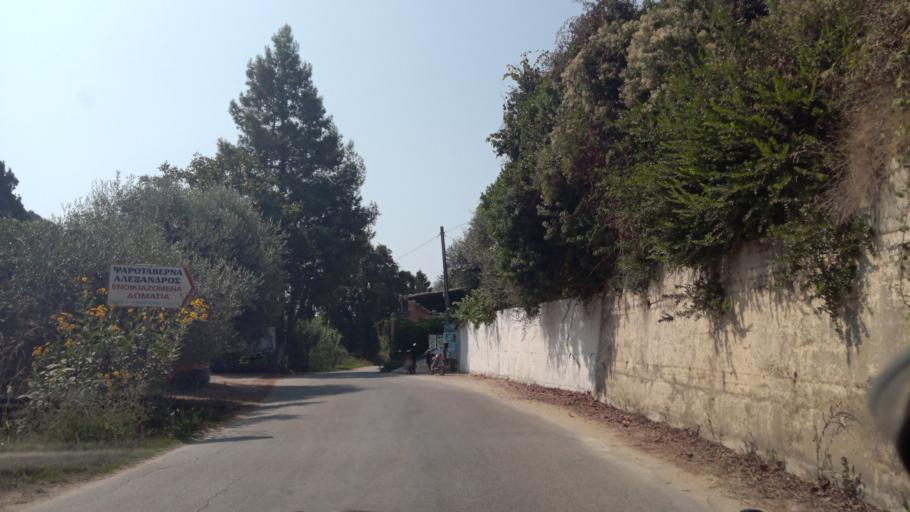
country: GR
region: Ionian Islands
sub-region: Nomos Kerkyras
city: Perivoli
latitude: 39.3999
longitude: 20.0246
